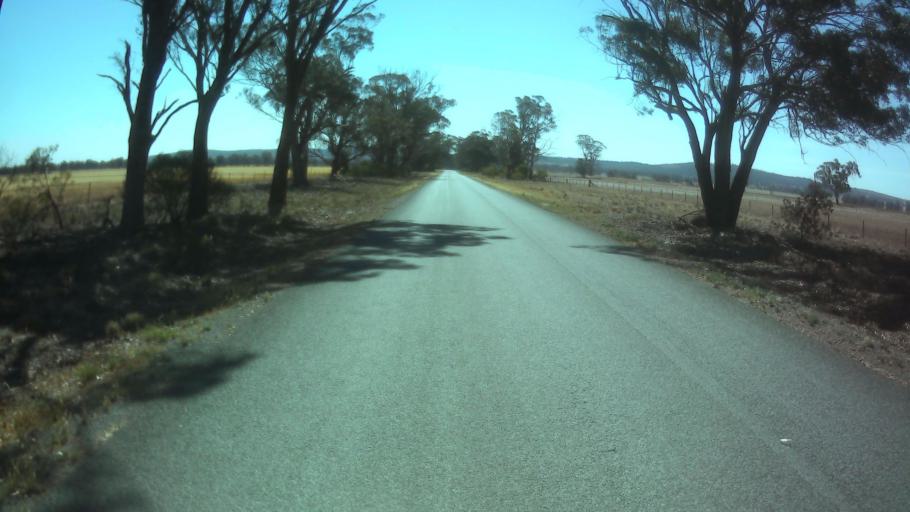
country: AU
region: New South Wales
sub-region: Weddin
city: Grenfell
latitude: -33.8127
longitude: 147.9230
